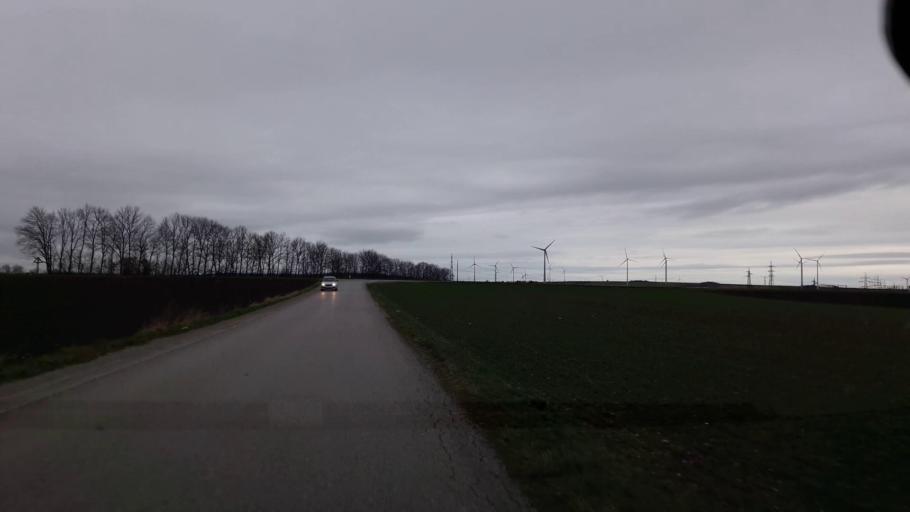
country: AT
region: Lower Austria
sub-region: Politischer Bezirk Bruck an der Leitha
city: Bruck an der Leitha
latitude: 48.0263
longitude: 16.7602
